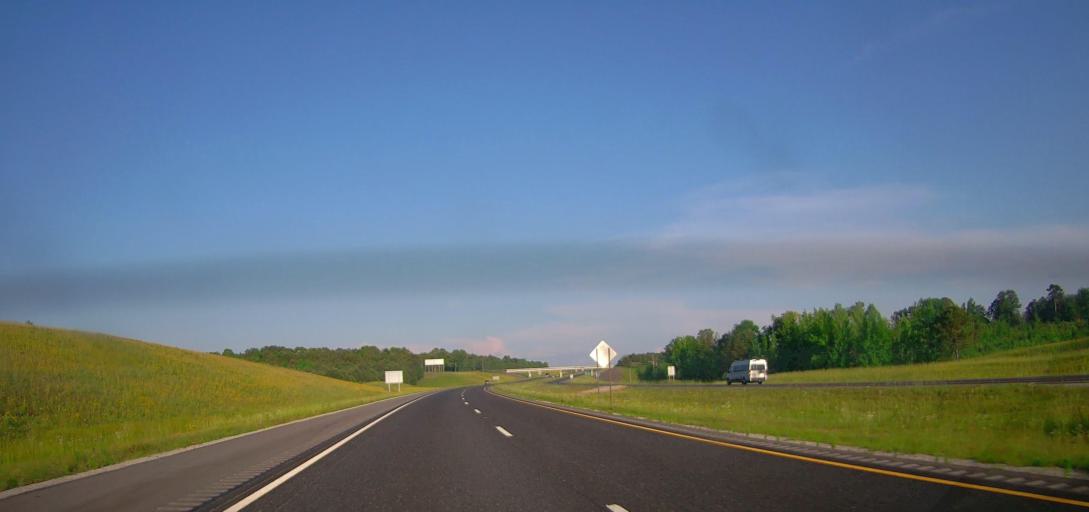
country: US
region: Alabama
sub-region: Marion County
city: Winfield
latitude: 33.9876
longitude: -87.7681
